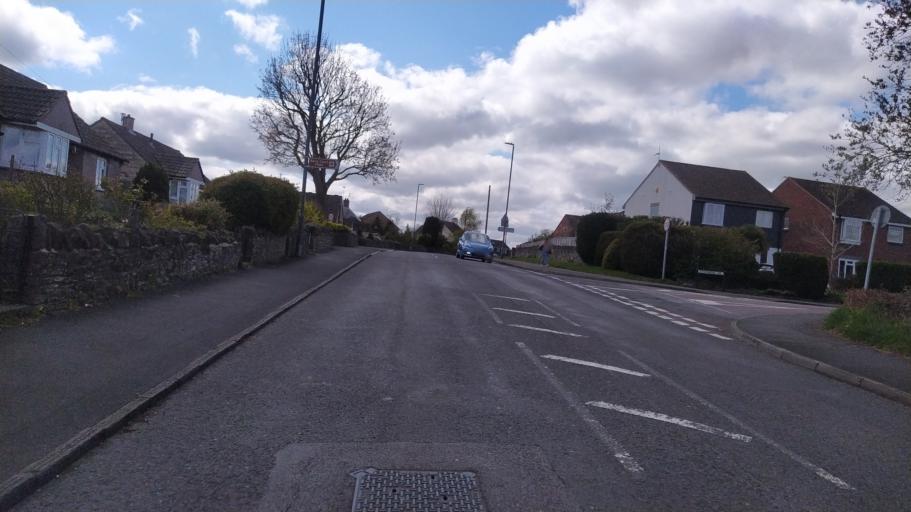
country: GB
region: England
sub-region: South Gloucestershire
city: Kingswood
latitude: 51.4459
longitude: -2.4882
